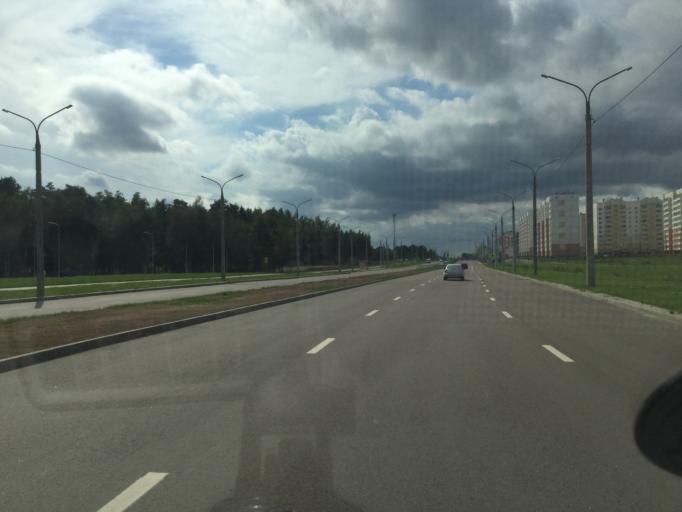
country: BY
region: Vitebsk
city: Vitebsk
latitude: 55.1681
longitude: 30.2951
